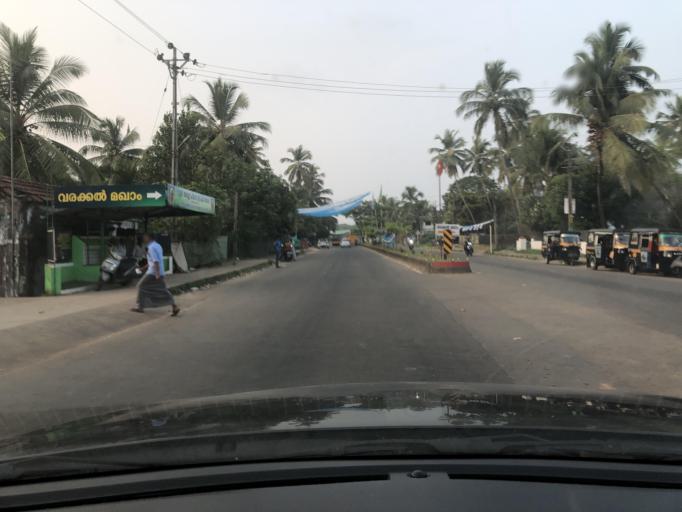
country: IN
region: Kerala
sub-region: Kozhikode
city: Kozhikode
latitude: 11.2990
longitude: 75.7558
